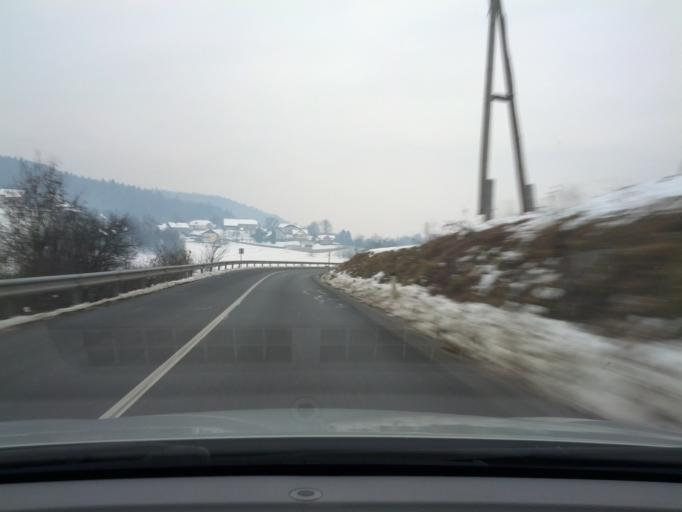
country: SI
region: Lukovica
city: Lukovica pri Domzalah
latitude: 46.1343
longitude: 14.6925
